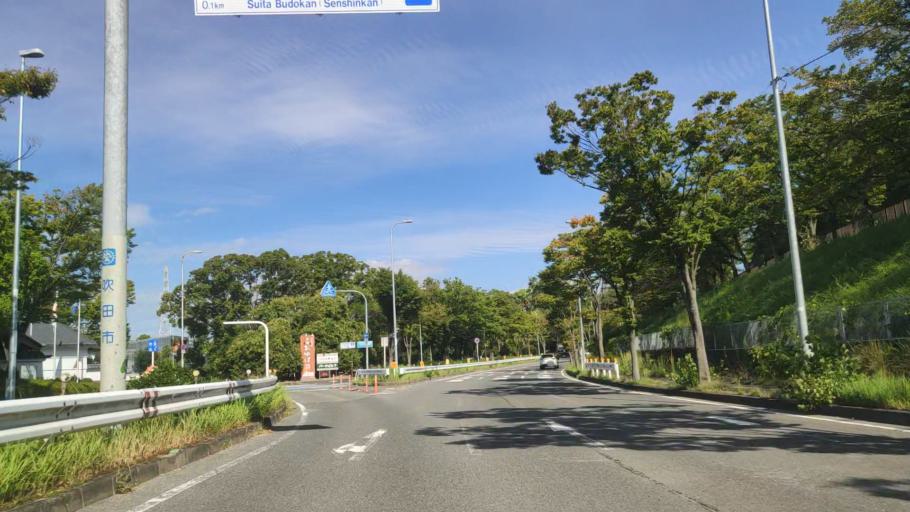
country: JP
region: Osaka
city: Suita
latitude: 34.8090
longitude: 135.5210
